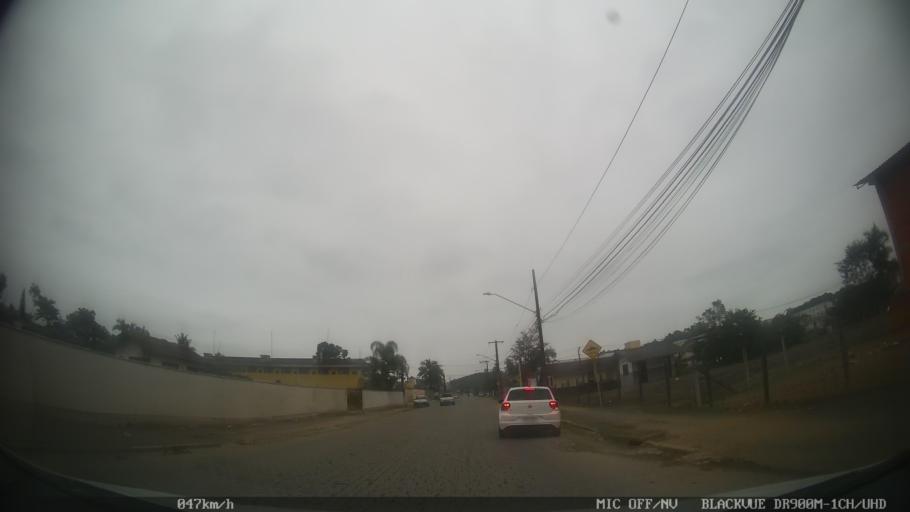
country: BR
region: Santa Catarina
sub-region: Joinville
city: Joinville
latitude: -26.3437
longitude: -48.8518
